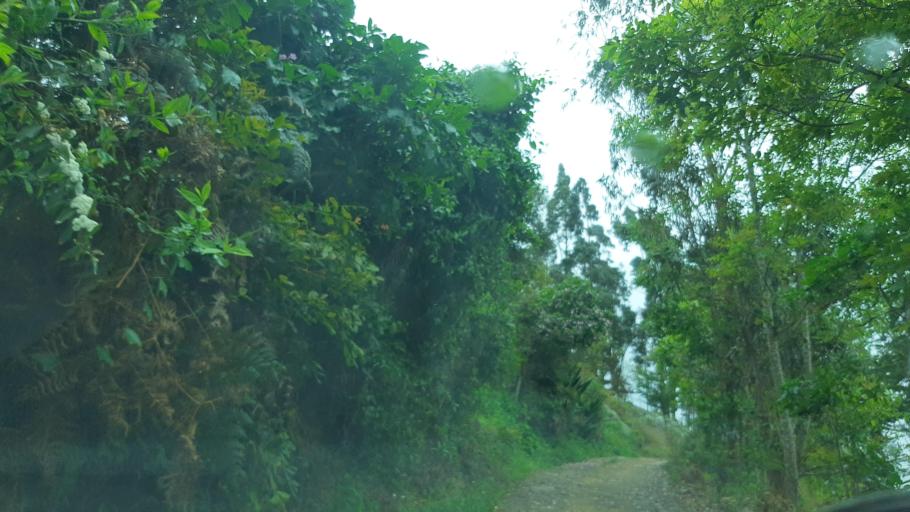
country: CO
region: Boyaca
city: Tibana
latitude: 5.3002
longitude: -73.4334
